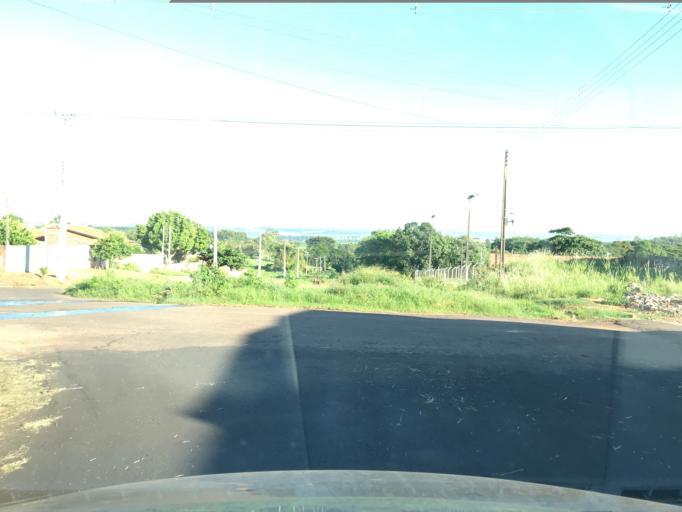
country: BR
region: Parana
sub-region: Ipora
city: Ipora
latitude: -23.9985
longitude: -53.7118
